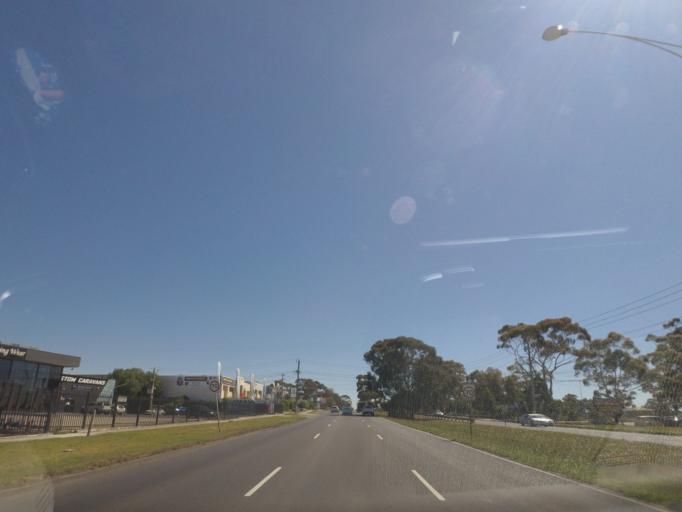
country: AU
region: Victoria
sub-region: Hume
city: Campbellfield
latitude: -37.6783
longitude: 144.9563
